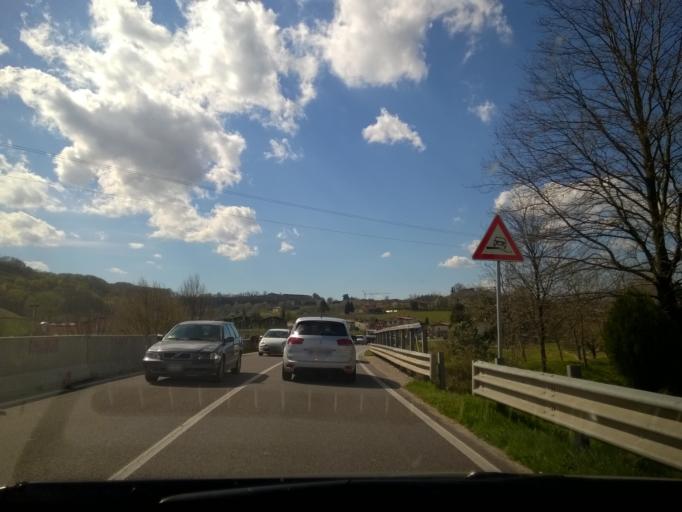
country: IT
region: Veneto
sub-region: Provincia di Treviso
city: Susegana
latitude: 45.8700
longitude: 12.2499
